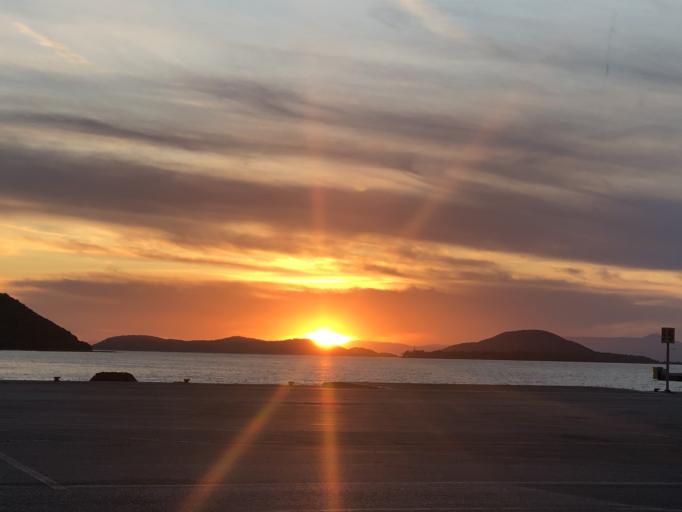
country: GR
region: Epirus
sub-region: Nomos Thesprotias
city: Igoumenitsa
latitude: 39.4883
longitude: 20.2586
